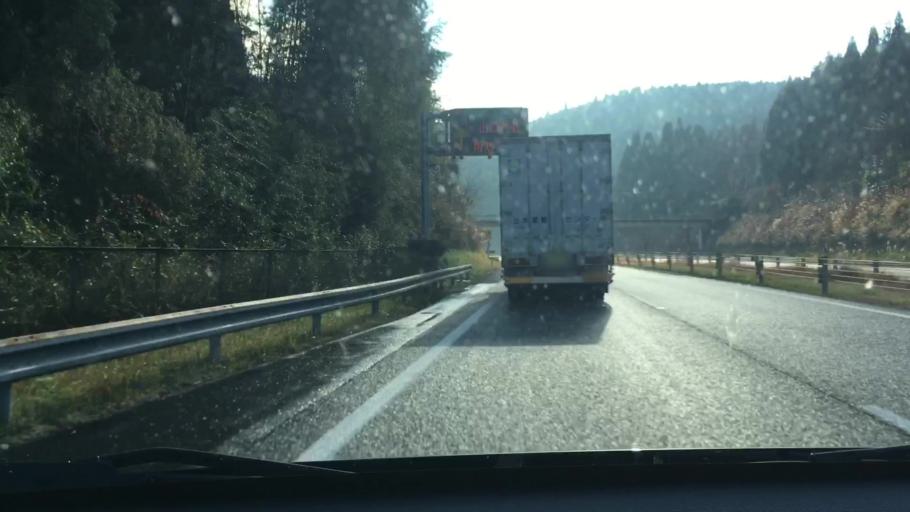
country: JP
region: Kagoshima
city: Okuchi-shinohara
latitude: 31.9853
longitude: 130.7532
